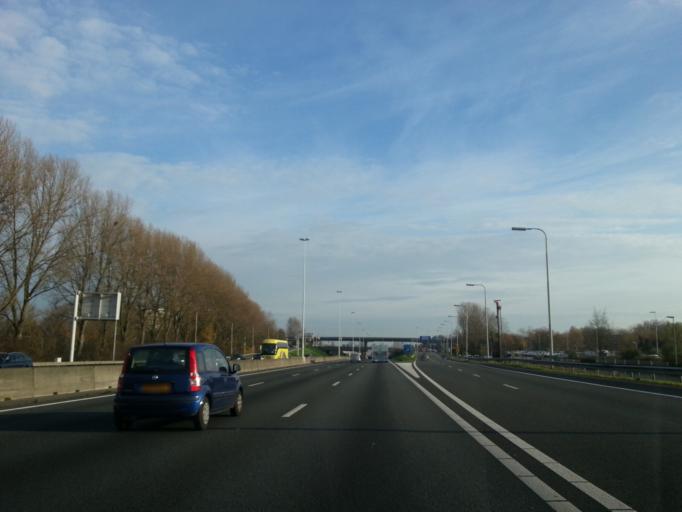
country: NL
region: South Holland
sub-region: Gemeente Rotterdam
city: Rotterdam
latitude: 51.9365
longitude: 4.4564
